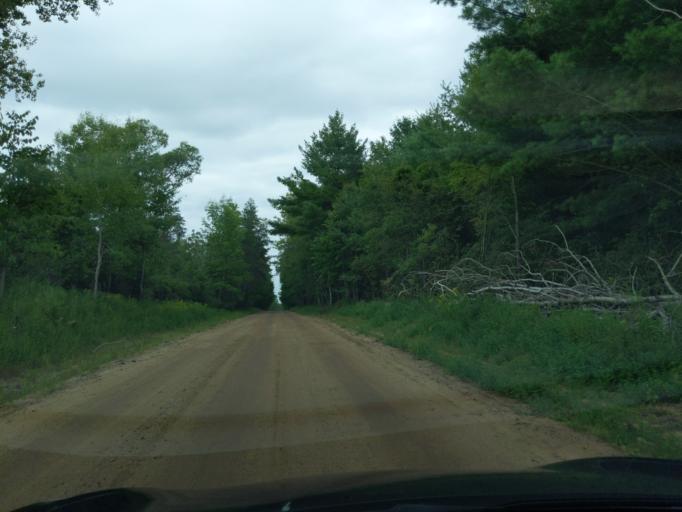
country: US
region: Michigan
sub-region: Clare County
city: Harrison
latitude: 43.9878
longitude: -85.0052
